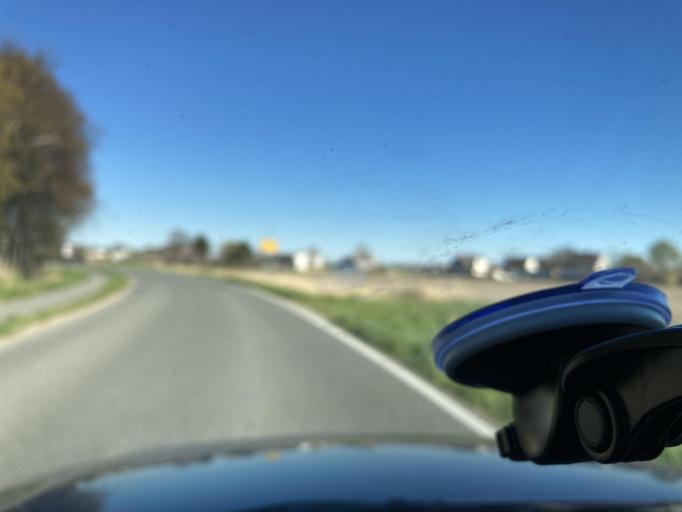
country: DE
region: Schleswig-Holstein
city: Neuenkirchen
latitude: 54.2356
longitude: 8.9856
